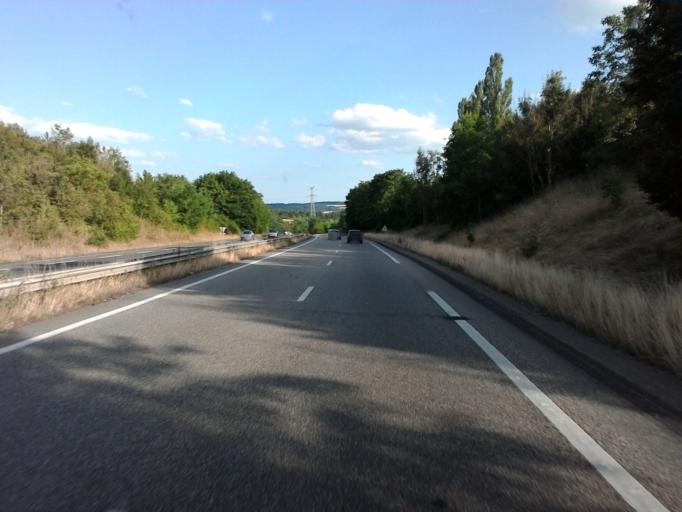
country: FR
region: Lorraine
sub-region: Departement de Meurthe-et-Moselle
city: Richardmenil
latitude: 48.5912
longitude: 6.1725
